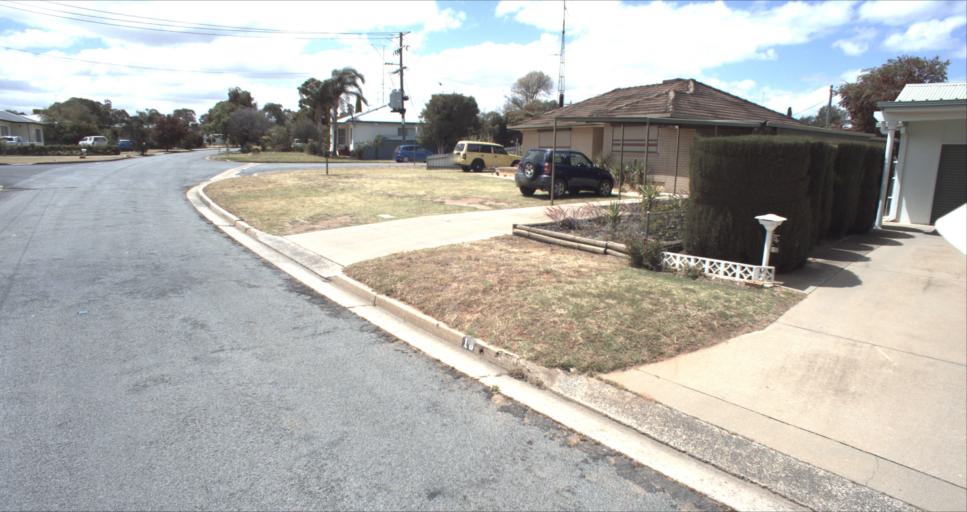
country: AU
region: New South Wales
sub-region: Leeton
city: Leeton
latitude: -34.5629
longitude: 146.3936
